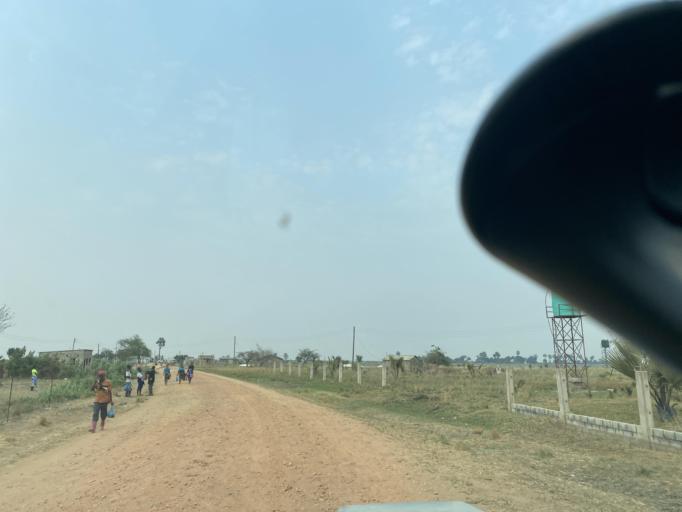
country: ZM
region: Lusaka
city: Kafue
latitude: -15.6860
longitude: 28.0077
